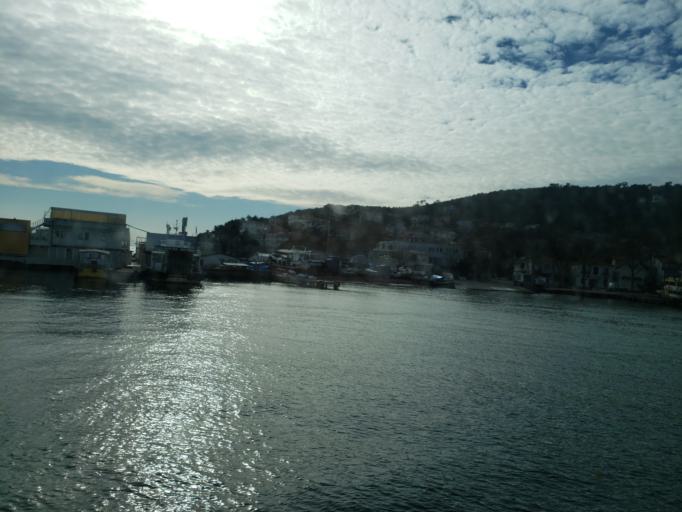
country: TR
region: Istanbul
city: Adalan
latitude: 40.8803
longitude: 29.0719
